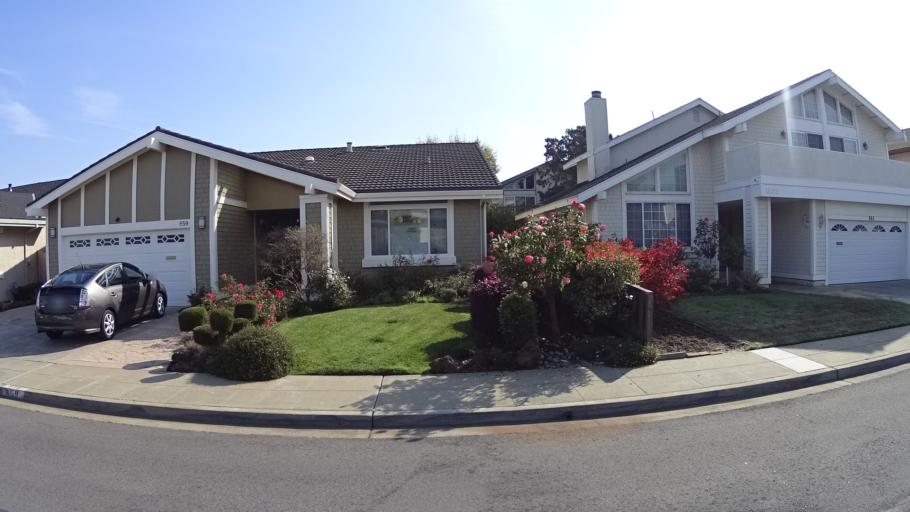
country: US
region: California
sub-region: San Mateo County
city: Foster City
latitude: 37.5465
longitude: -122.2767
